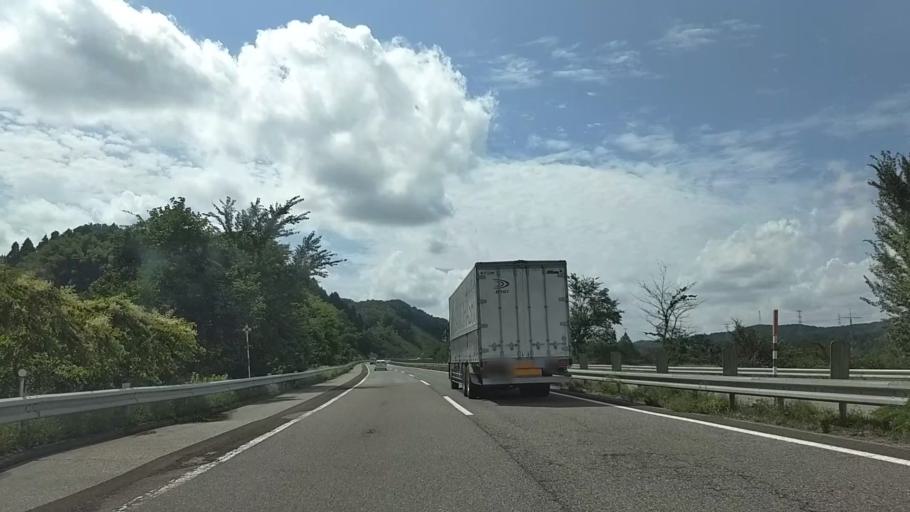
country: JP
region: Toyama
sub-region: Oyabe Shi
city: Oyabe
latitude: 36.6210
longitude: 136.8263
